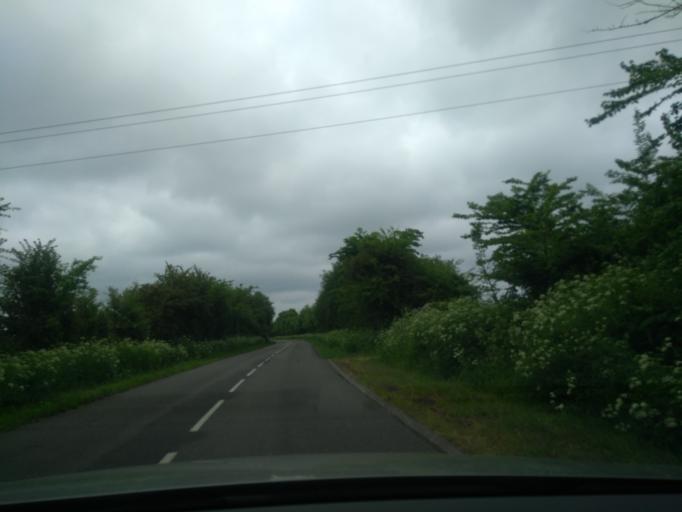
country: FR
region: Lower Normandy
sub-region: Departement de la Manche
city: Sainte-Mere-Eglise
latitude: 49.4616
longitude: -1.2611
